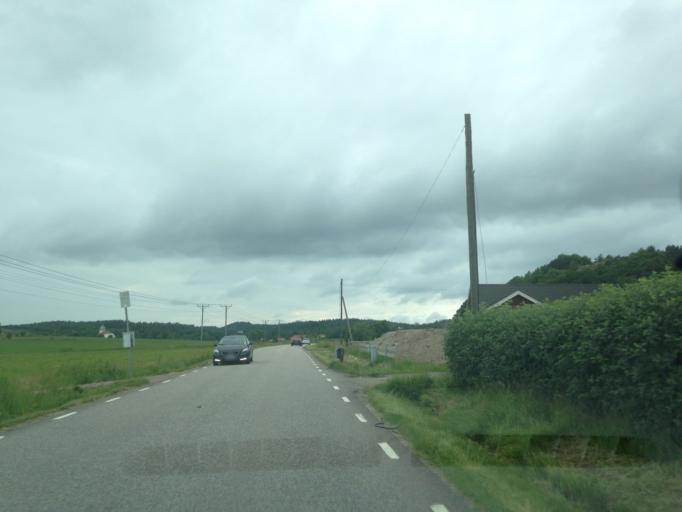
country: SE
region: Vaestra Goetaland
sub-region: Kungalvs Kommun
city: Kode
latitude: 57.8360
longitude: 11.7969
